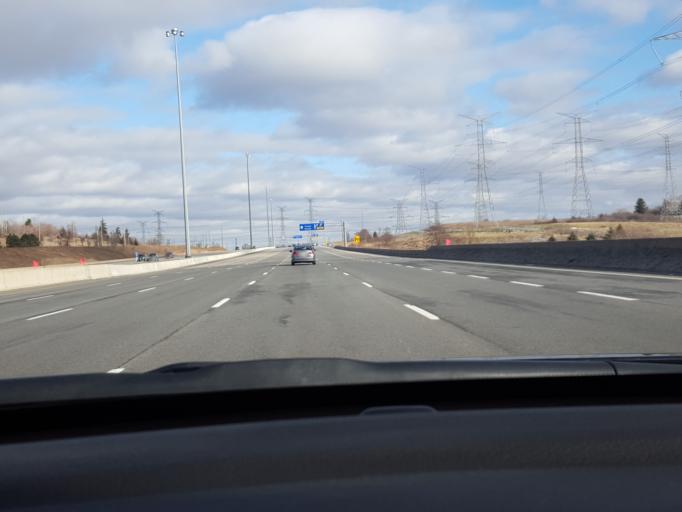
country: CA
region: Ontario
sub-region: York
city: Richmond Hill
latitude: 43.8301
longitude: -79.4421
